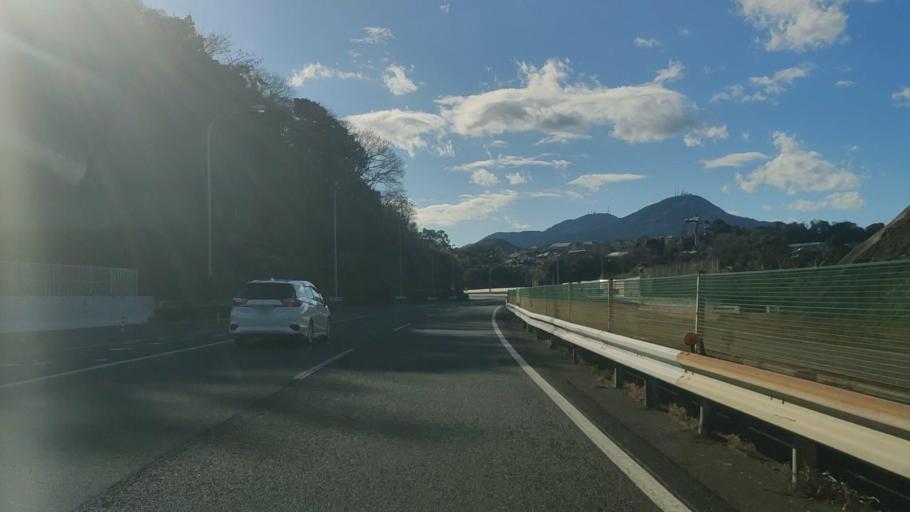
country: JP
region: Fukuoka
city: Kitakyushu
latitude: 33.8585
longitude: 130.8460
